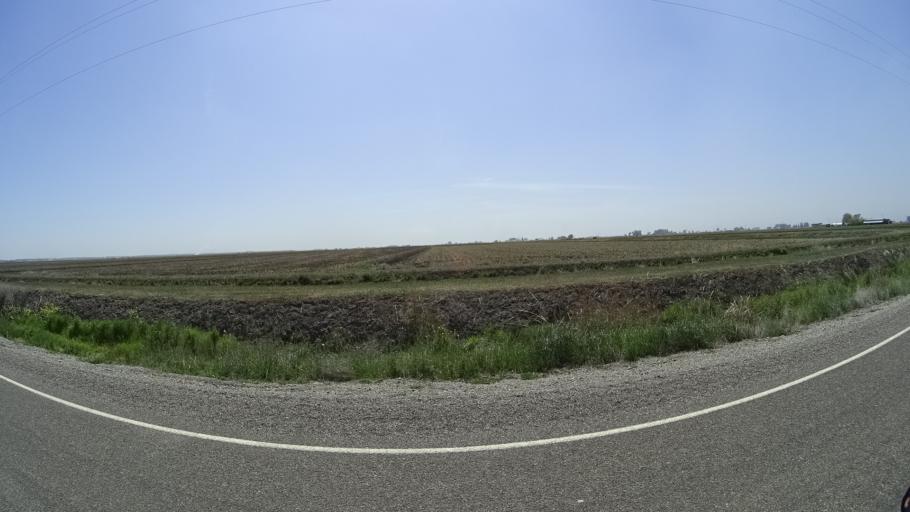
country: US
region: California
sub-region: Glenn County
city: Willows
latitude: 39.5582
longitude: -122.0780
